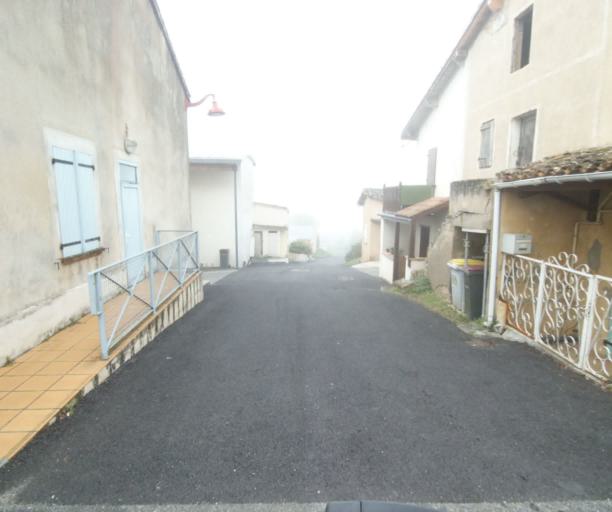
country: FR
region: Midi-Pyrenees
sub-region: Departement du Tarn-et-Garonne
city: Nohic
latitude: 43.9327
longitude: 1.4596
